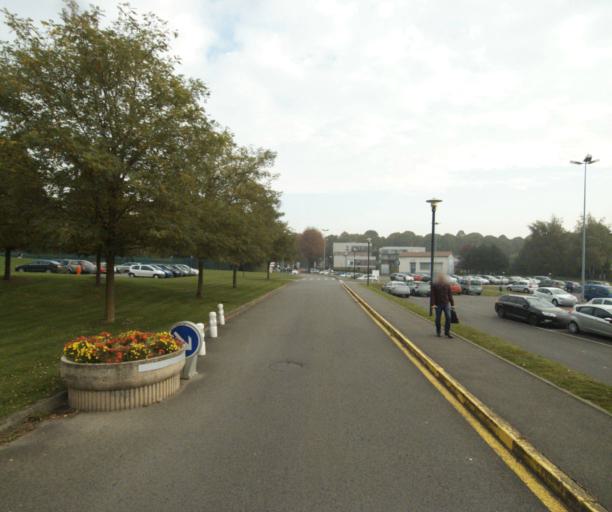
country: FR
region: Nord-Pas-de-Calais
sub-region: Departement du Nord
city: Seclin
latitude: 50.5460
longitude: 3.0191
